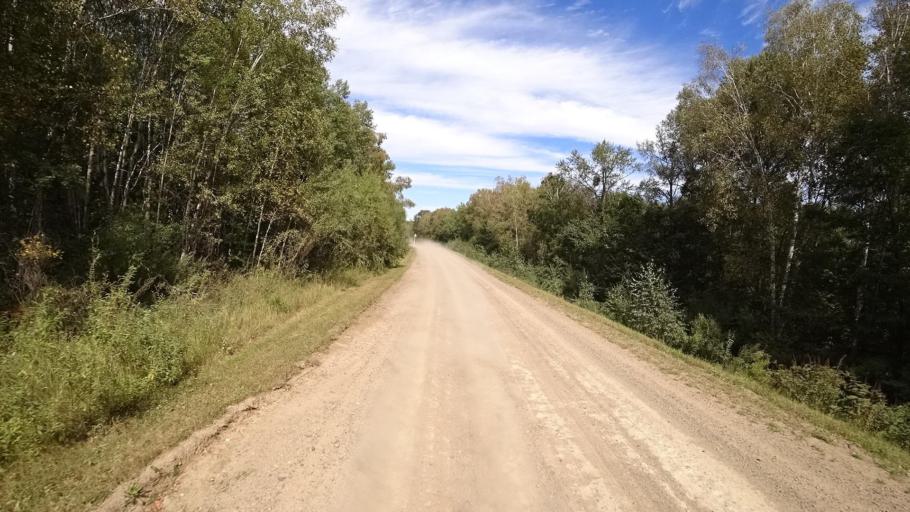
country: RU
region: Primorskiy
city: Yakovlevka
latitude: 44.6664
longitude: 133.6101
